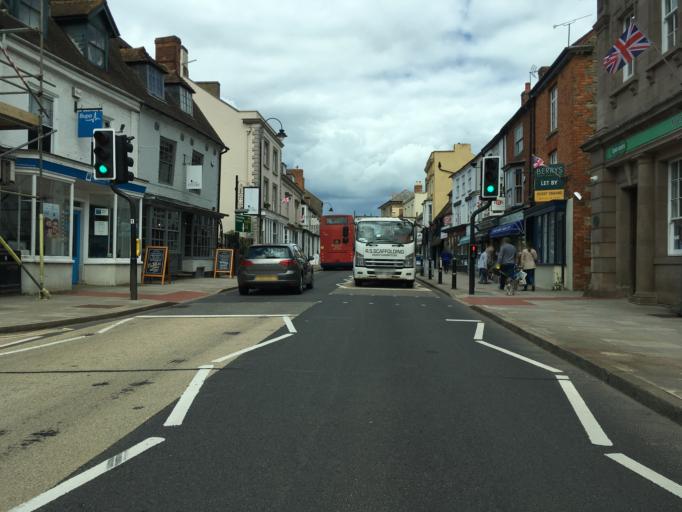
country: GB
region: England
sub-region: Northamptonshire
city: Towcester
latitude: 52.1327
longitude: -0.9893
